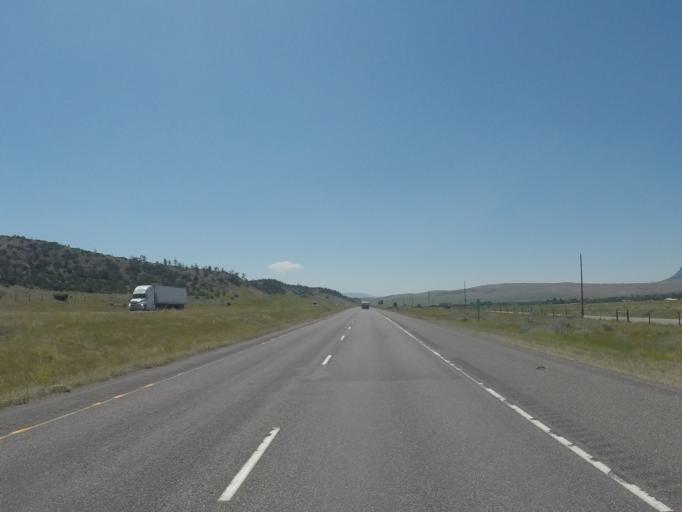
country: US
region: Montana
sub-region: Sweet Grass County
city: Big Timber
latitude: 45.7407
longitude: -110.2007
